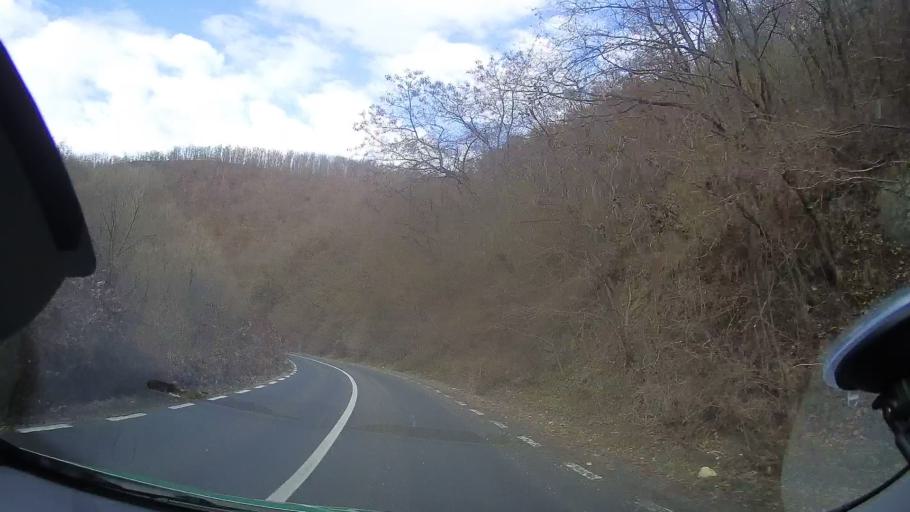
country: RO
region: Cluj
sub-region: Comuna Baisoara
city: Baisoara
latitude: 46.5873
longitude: 23.4481
